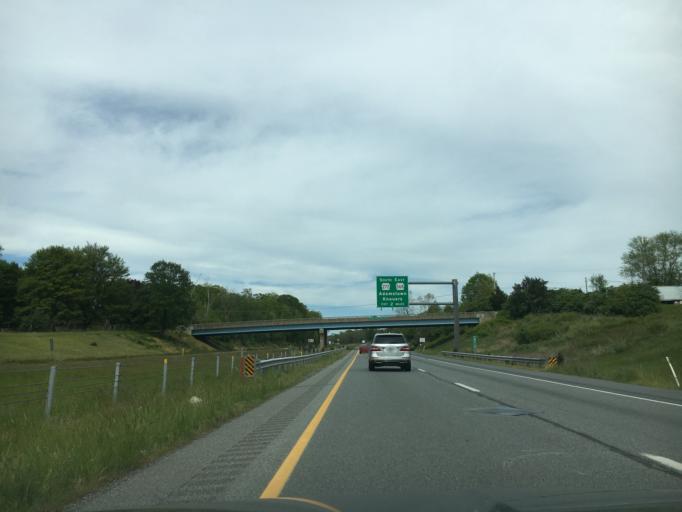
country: US
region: Pennsylvania
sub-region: Lancaster County
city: Swartzville
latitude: 40.2236
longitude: -76.0661
